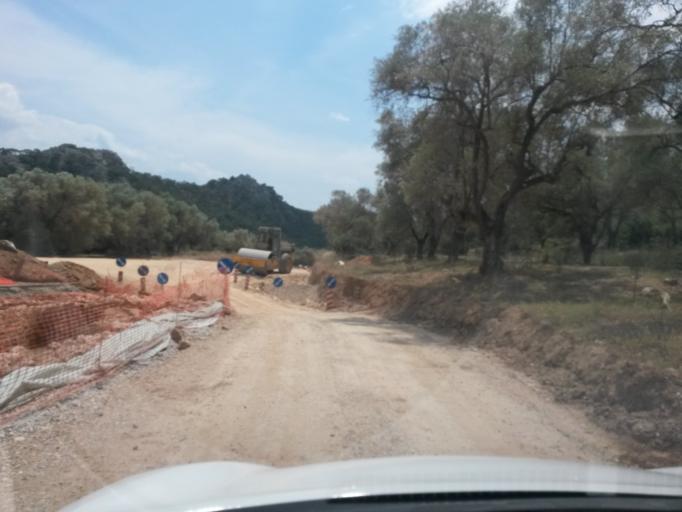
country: GR
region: North Aegean
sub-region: Nomos Lesvou
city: Pamfylla
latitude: 39.1756
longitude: 26.4246
